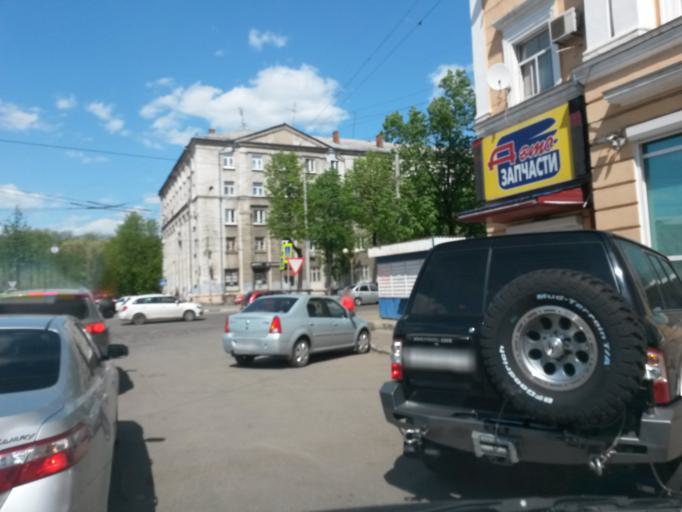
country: RU
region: Jaroslavl
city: Yaroslavl
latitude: 57.6339
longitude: 39.8612
